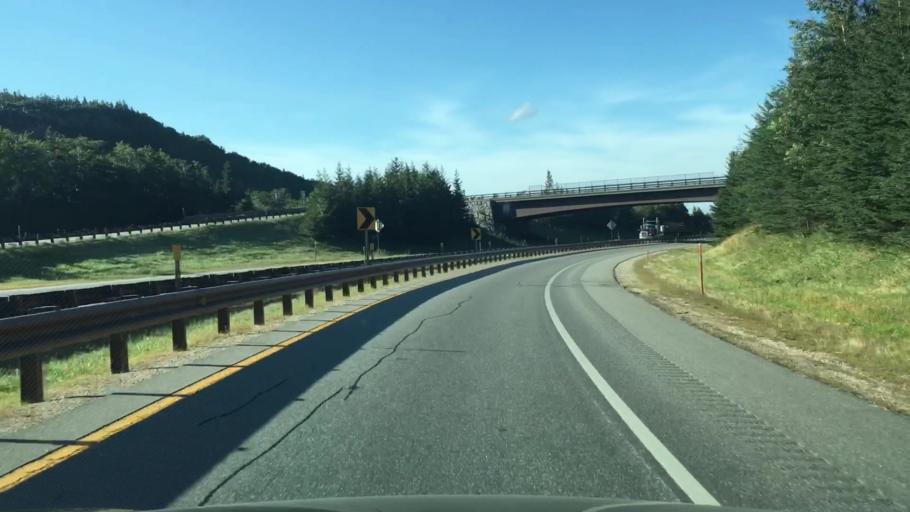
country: US
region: New Hampshire
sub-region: Grafton County
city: Deerfield
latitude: 44.1781
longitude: -71.6917
